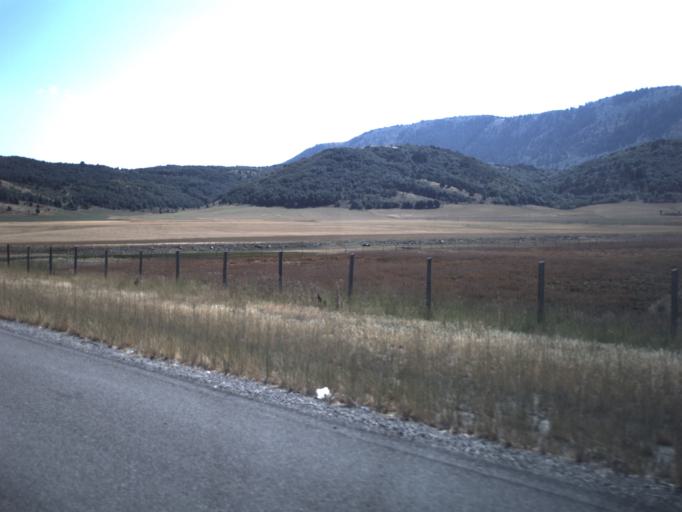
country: US
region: Utah
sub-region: Box Elder County
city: Brigham City
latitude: 41.5657
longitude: -111.9652
